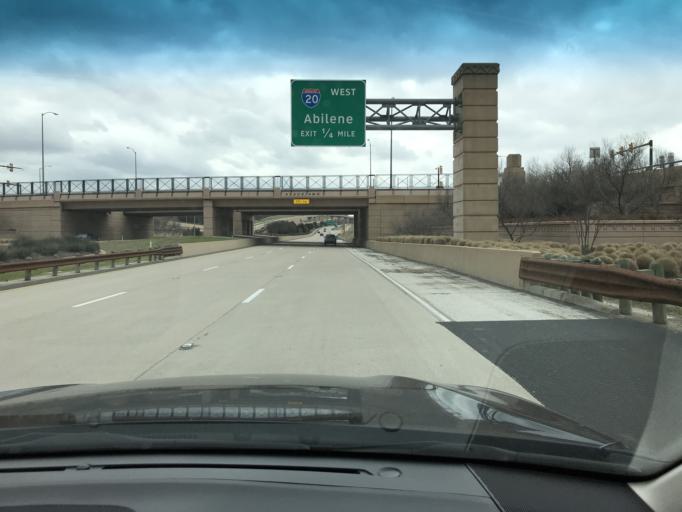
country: US
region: Texas
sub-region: Tarrant County
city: Westworth
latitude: 32.6996
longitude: -97.4062
